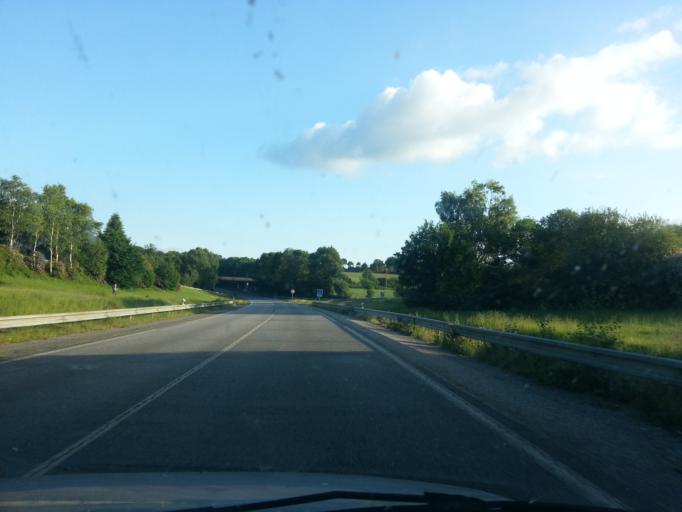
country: FR
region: Brittany
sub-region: Departement du Morbihan
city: Gourin
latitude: 48.1404
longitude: -3.5796
